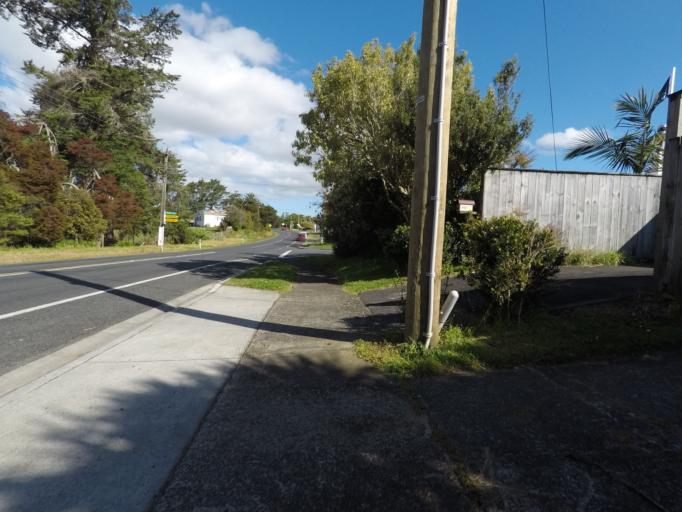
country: NZ
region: Auckland
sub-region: Auckland
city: Rosebank
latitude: -36.8565
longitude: 174.6039
